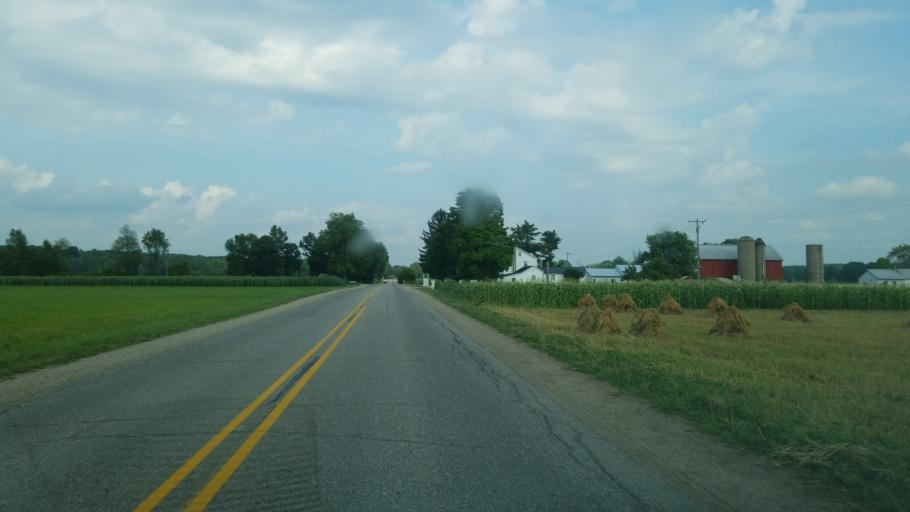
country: US
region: Michigan
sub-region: Mecosta County
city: Canadian Lakes
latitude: 43.5424
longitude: -85.3407
